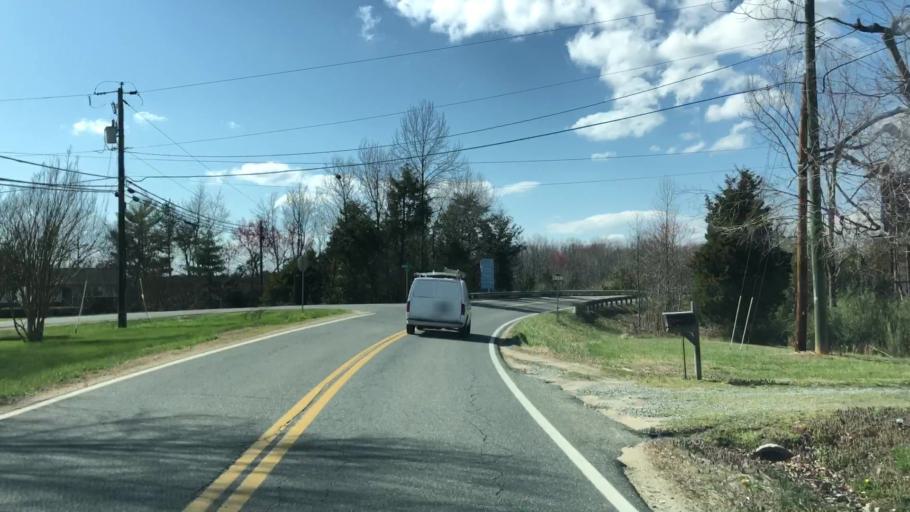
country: US
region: Virginia
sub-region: Stafford County
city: Falmouth
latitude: 38.3509
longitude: -77.4775
